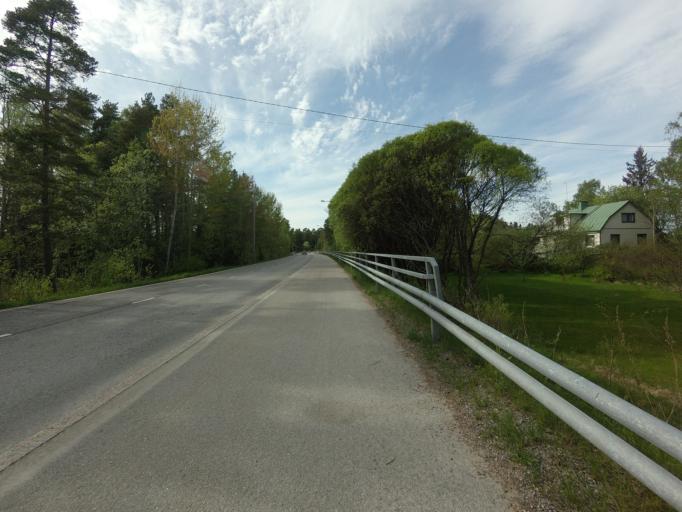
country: FI
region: Uusimaa
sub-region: Helsinki
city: Koukkuniemi
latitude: 60.1213
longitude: 24.7165
